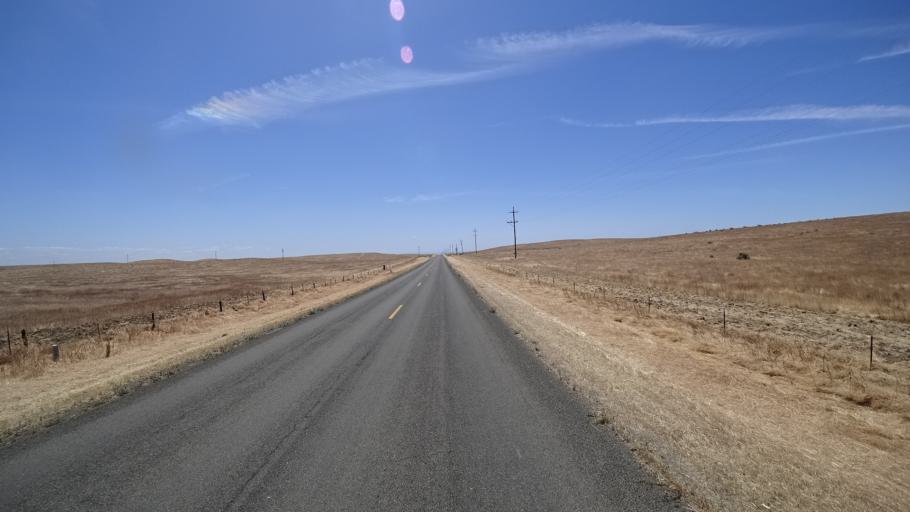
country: US
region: California
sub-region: Kings County
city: Kettleman City
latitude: 35.8796
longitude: -119.9152
